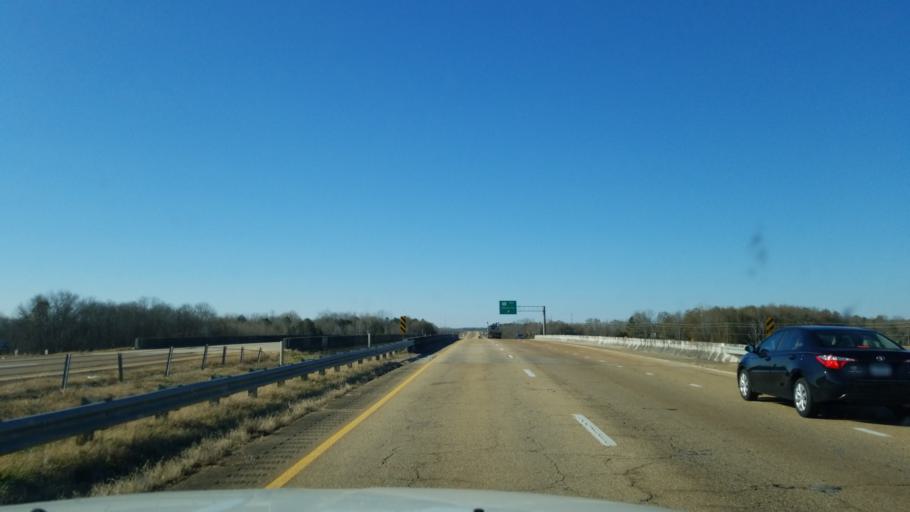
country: US
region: Mississippi
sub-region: Oktibbeha County
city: Starkville
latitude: 33.4719
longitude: -88.7603
